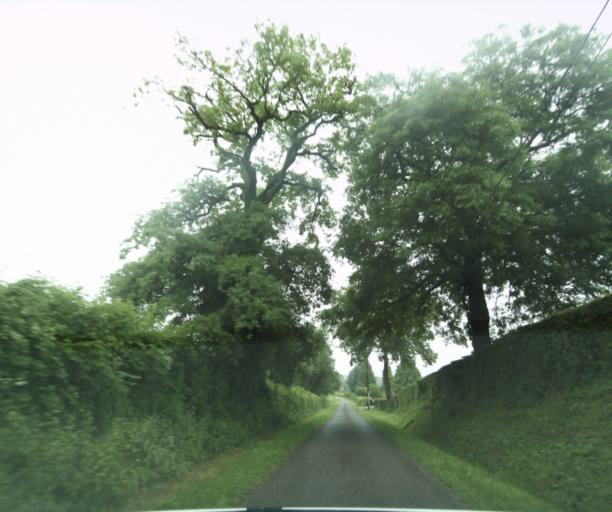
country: FR
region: Bourgogne
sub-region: Departement de Saone-et-Loire
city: Paray-le-Monial
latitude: 46.4009
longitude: 4.1910
